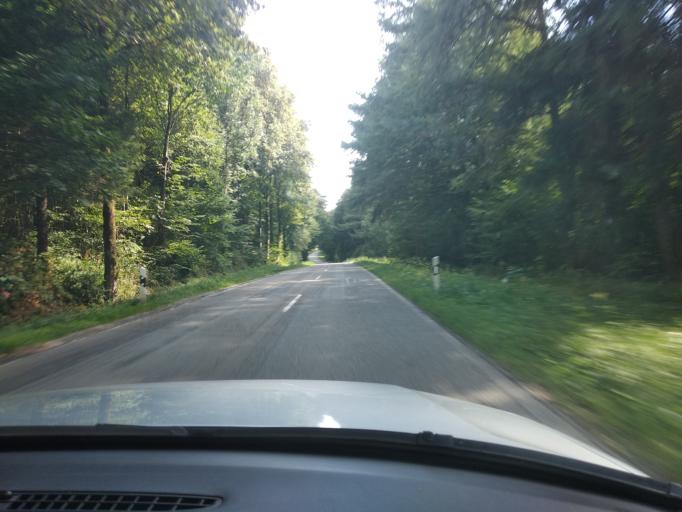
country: DE
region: Baden-Wuerttemberg
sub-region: Tuebingen Region
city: Leutkirch im Allgau
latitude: 47.8761
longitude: 9.9936
